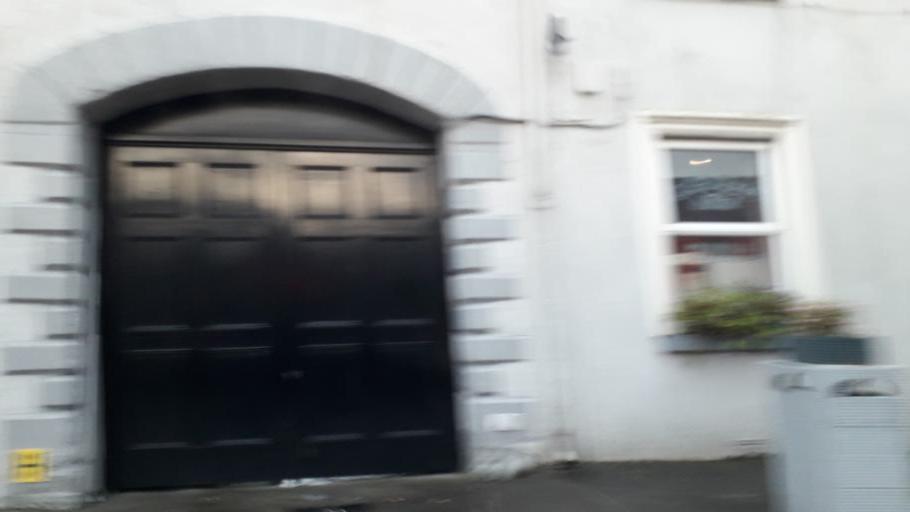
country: IE
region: Leinster
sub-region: An Longfort
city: Edgeworthstown
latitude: 53.6950
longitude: -7.6076
